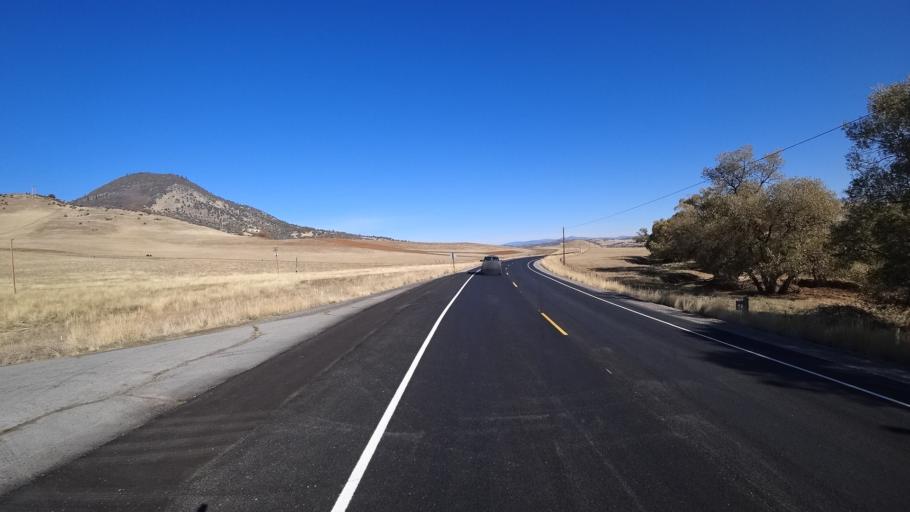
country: US
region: California
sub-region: Siskiyou County
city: Montague
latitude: 41.8283
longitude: -122.4935
